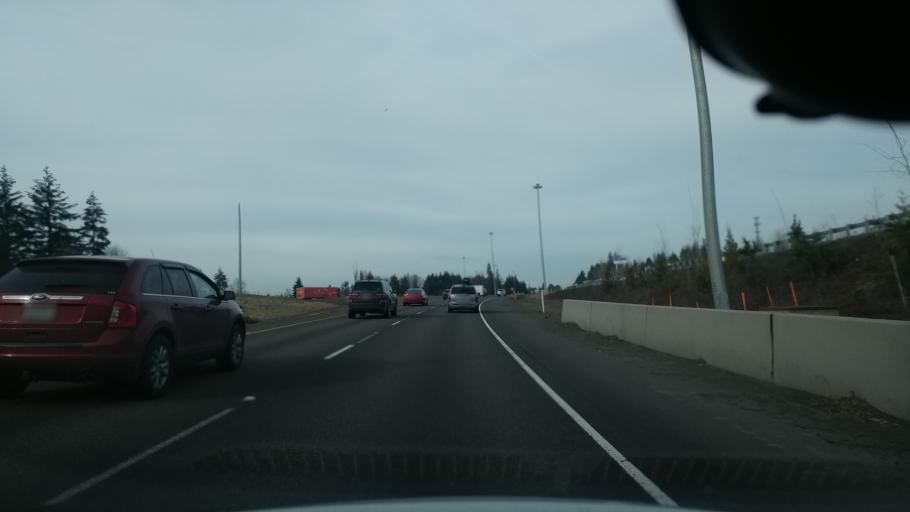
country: US
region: Washington
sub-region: Clark County
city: Salmon Creek
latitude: 45.7218
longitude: -122.6531
